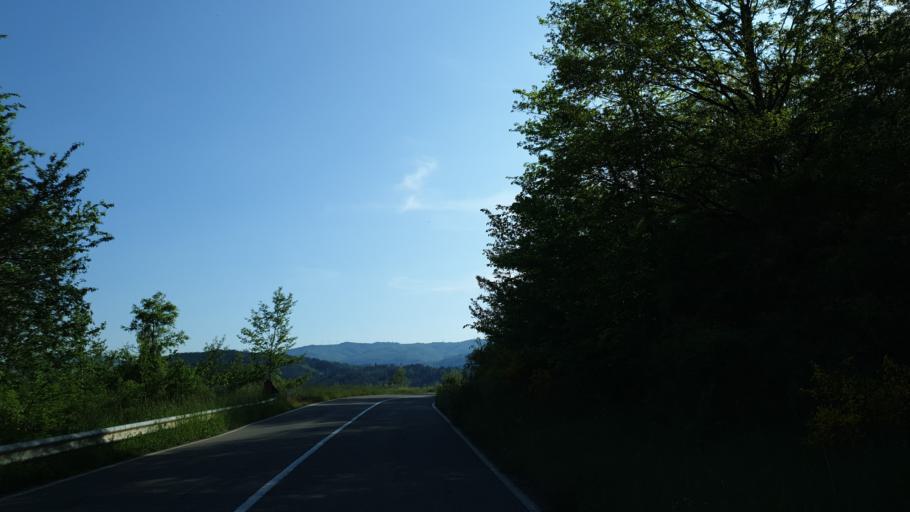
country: IT
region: Tuscany
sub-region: Province of Arezzo
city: Montemignaio
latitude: 43.7820
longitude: 11.6547
